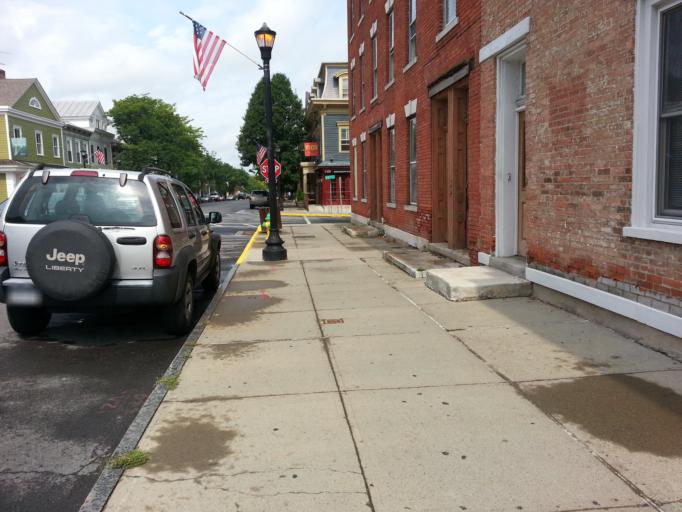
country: US
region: New York
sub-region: Columbia County
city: Hudson
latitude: 42.2544
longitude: -73.7930
